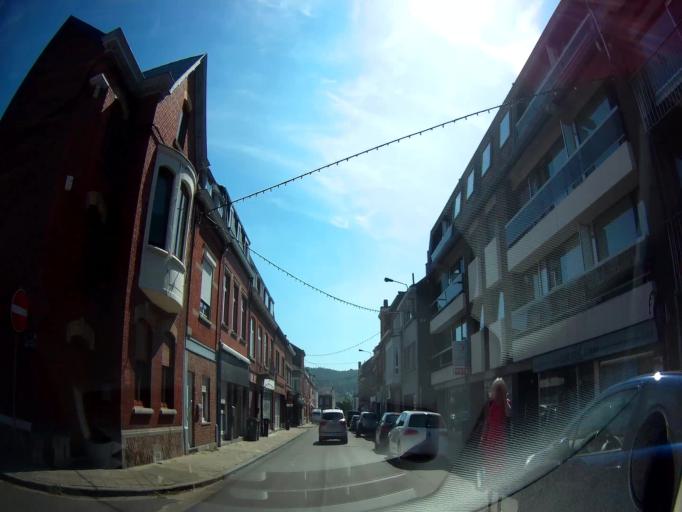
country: BE
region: Wallonia
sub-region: Province de Liege
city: Amay
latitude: 50.5474
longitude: 5.3200
